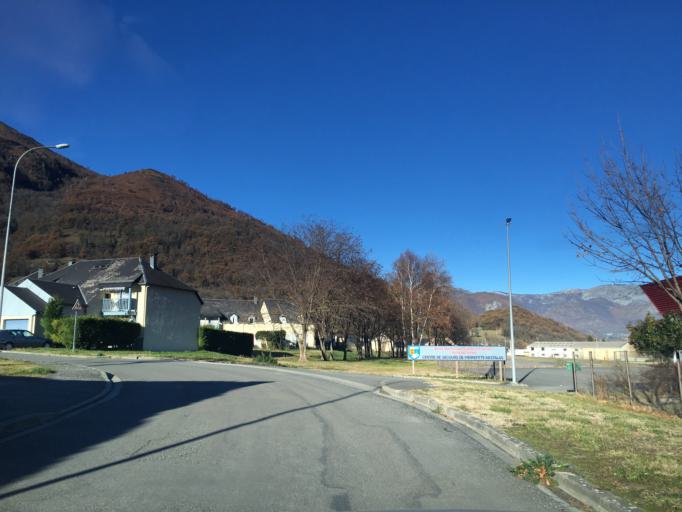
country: FR
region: Midi-Pyrenees
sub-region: Departement des Hautes-Pyrenees
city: Pierrefitte-Nestalas
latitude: 42.9628
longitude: -0.0688
